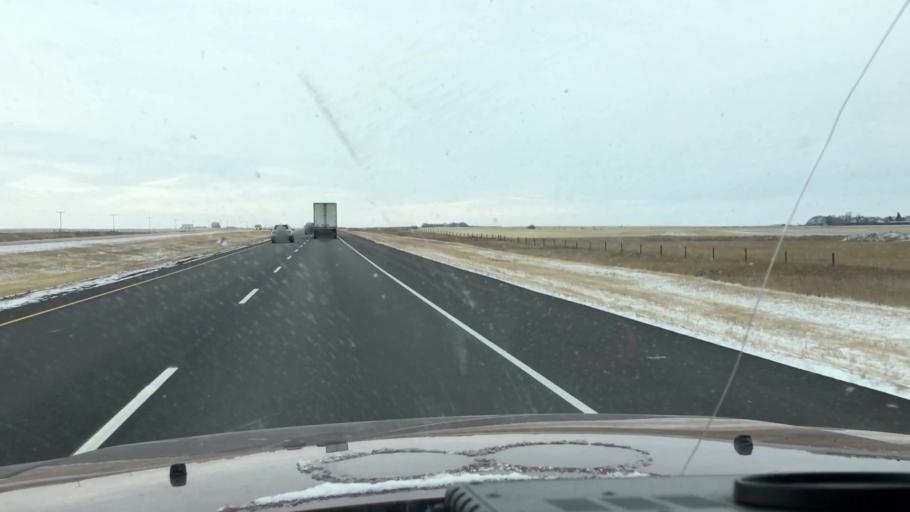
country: CA
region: Saskatchewan
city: Saskatoon
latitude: 51.8015
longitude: -106.4904
